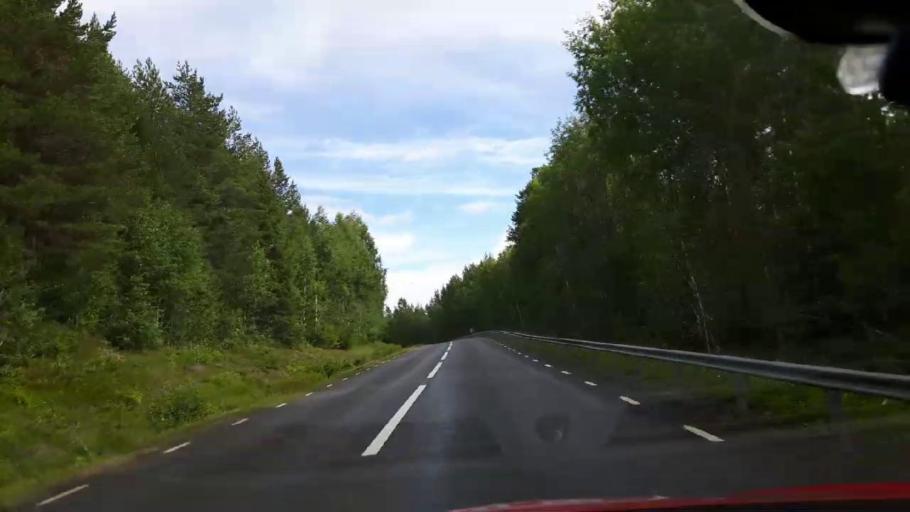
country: SE
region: Jaemtland
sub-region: Stroemsunds Kommun
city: Stroemsund
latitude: 64.3391
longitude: 14.9174
